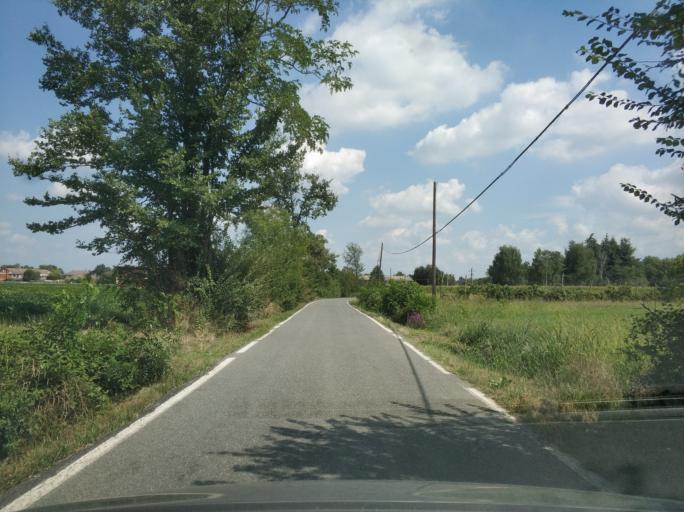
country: IT
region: Piedmont
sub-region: Provincia di Torino
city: Rivarossa
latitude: 45.2466
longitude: 7.6922
